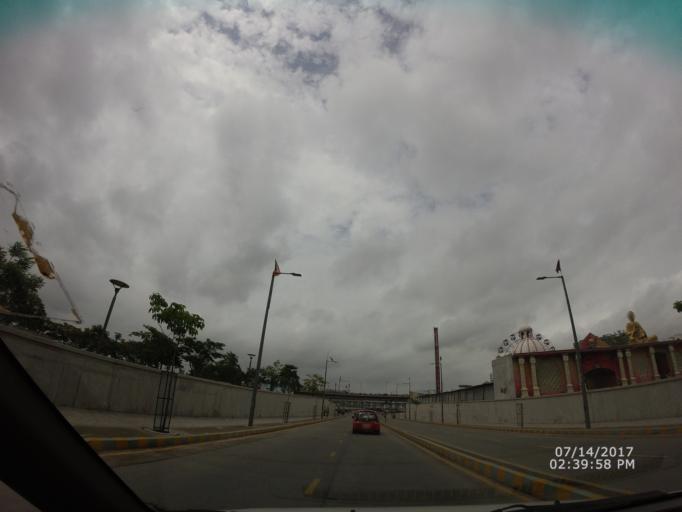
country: IN
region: Gujarat
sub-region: Ahmadabad
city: Ahmedabad
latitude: 23.0590
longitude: 72.5852
